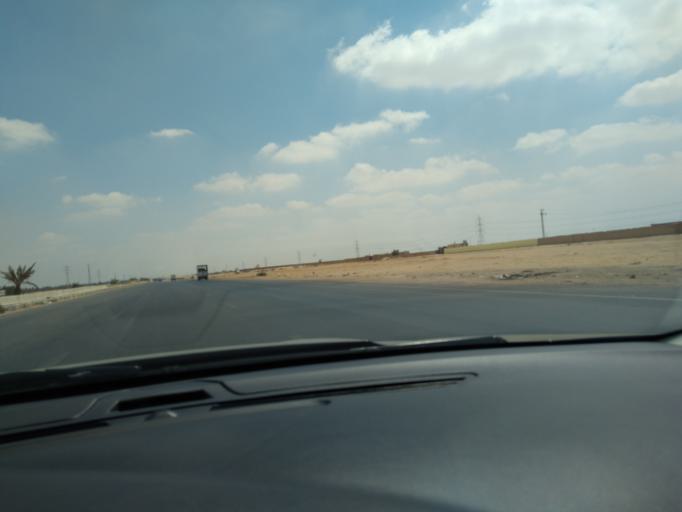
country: EG
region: Al Isma'iliyah
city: At Tall al Kabir
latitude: 30.3464
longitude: 31.8765
